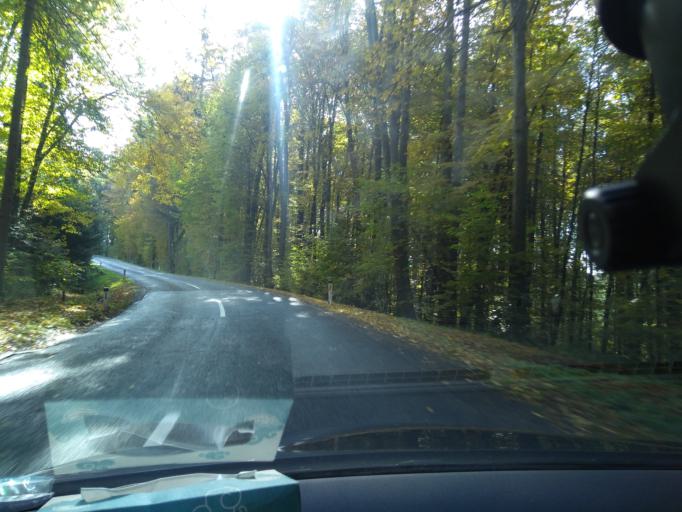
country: AT
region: Styria
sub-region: Politischer Bezirk Leibnitz
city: Sankt Ulrich am Waasen
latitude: 46.9246
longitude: 15.5318
